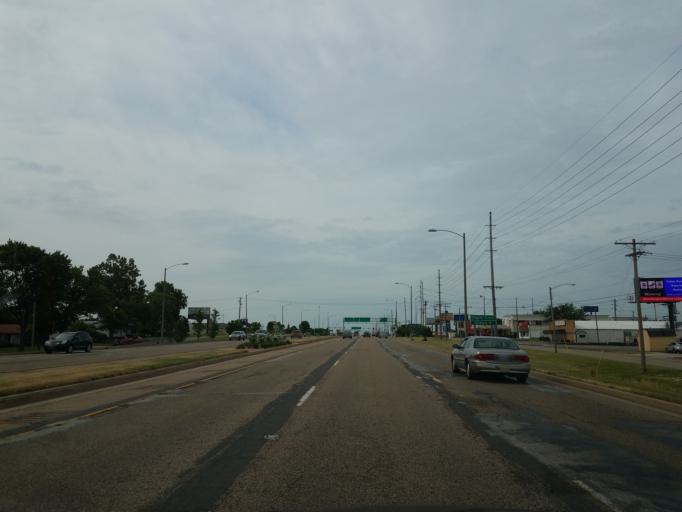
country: US
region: Illinois
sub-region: McLean County
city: Bloomington
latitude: 40.4932
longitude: -88.9531
